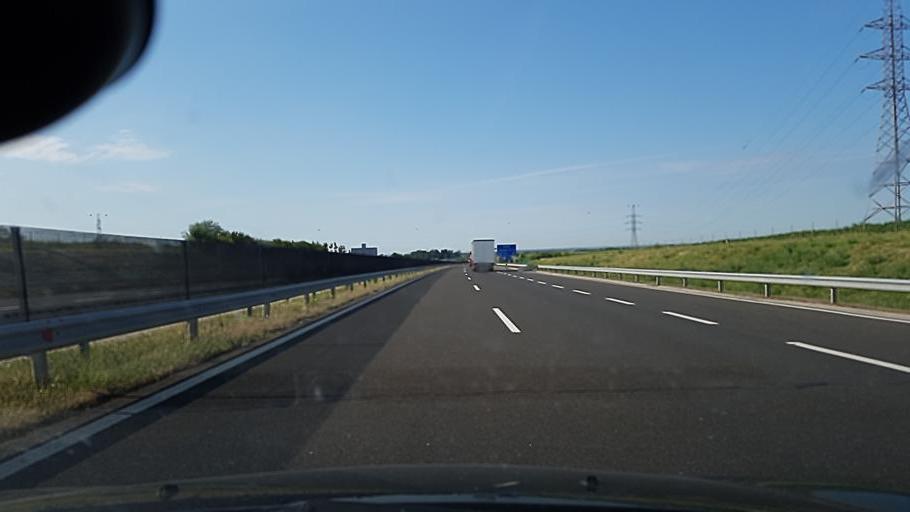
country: HU
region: Fejer
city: dunaujvaros
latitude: 46.9569
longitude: 18.8931
